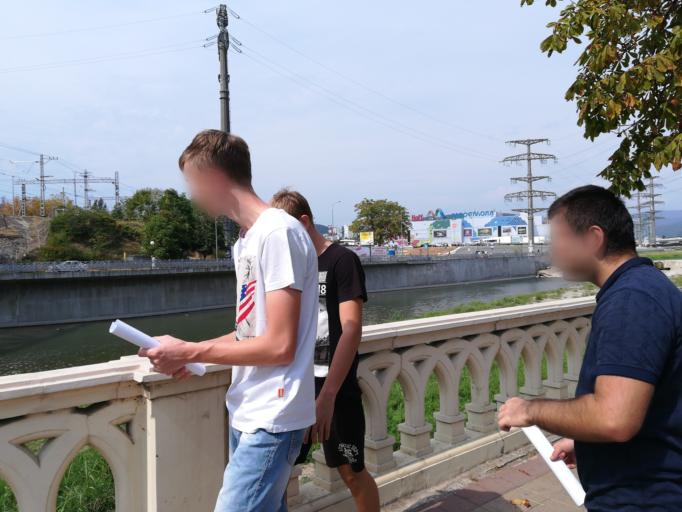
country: RU
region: Krasnodarskiy
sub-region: Sochi City
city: Sochi
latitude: 43.6006
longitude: 39.7311
